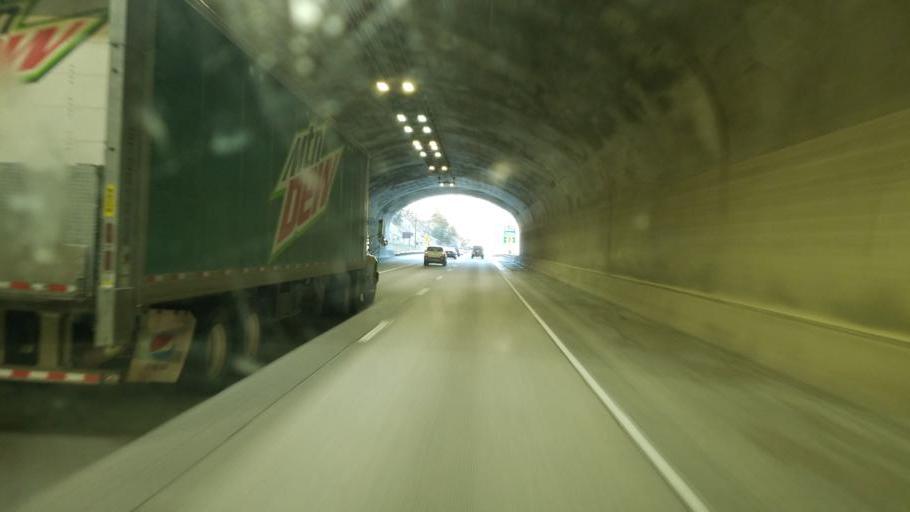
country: US
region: Colorado
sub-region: Clear Creek County
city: Idaho Springs
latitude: 39.7448
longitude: -105.4748
